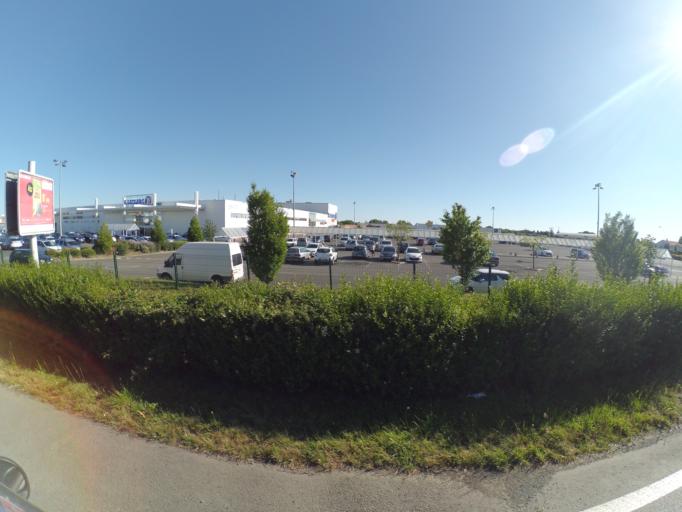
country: FR
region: Pays de la Loire
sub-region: Departement de la Vendee
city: Les Herbiers
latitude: 46.8583
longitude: -1.0136
